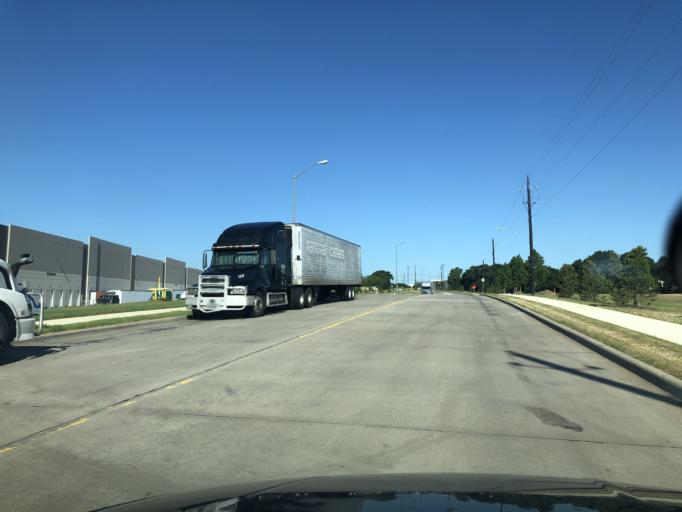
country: US
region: Texas
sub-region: Tarrant County
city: Euless
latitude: 32.8215
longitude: -97.0269
